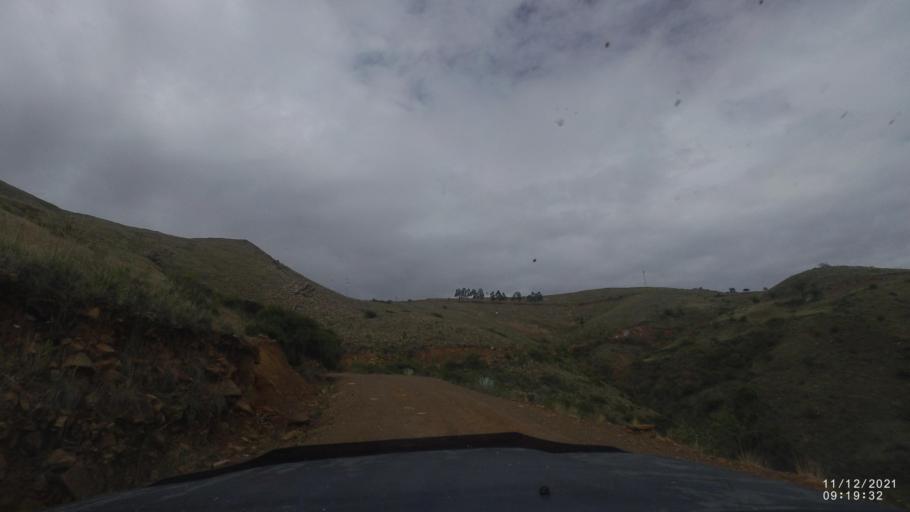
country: BO
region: Cochabamba
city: Tarata
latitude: -17.8814
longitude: -65.9716
